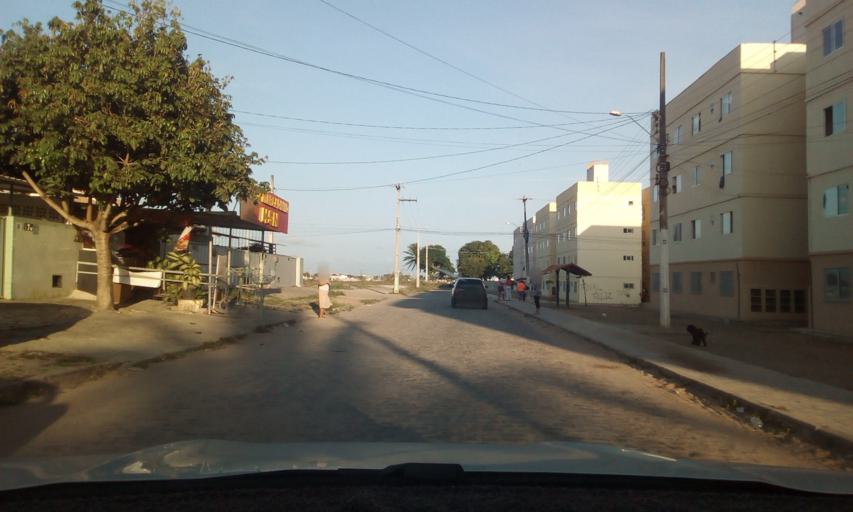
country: BR
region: Paraiba
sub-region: Bayeux
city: Bayeux
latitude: -7.1827
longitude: -34.9321
